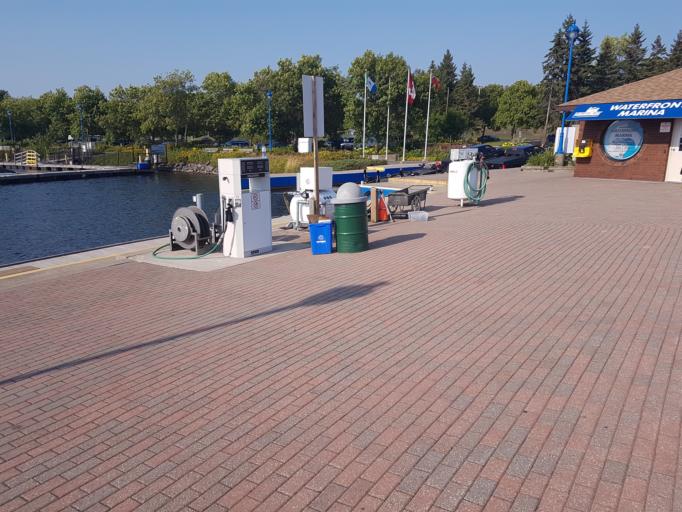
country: CA
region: Ontario
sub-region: Nipissing District
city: North Bay
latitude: 46.3109
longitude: -79.4704
